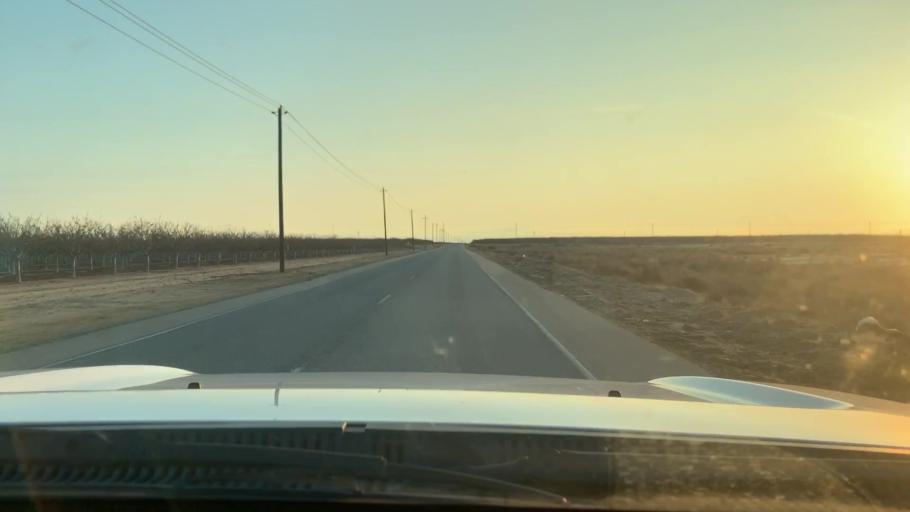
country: US
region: California
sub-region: Kern County
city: Buttonwillow
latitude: 35.5004
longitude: -119.4461
